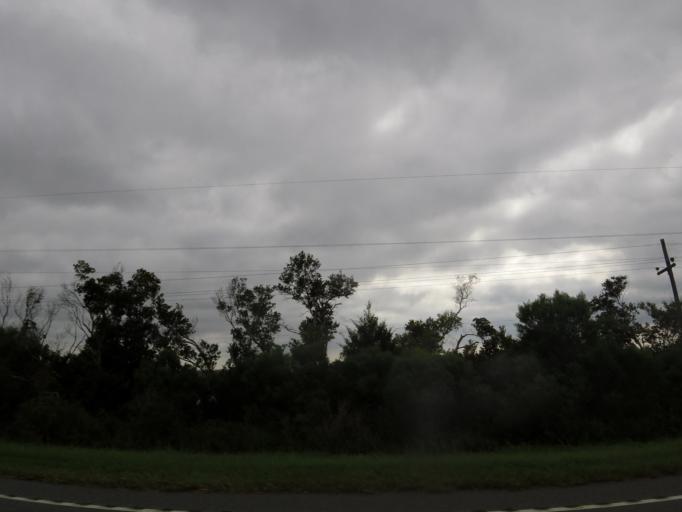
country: US
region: Georgia
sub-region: Glynn County
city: Brunswick
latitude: 31.0734
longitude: -81.4657
